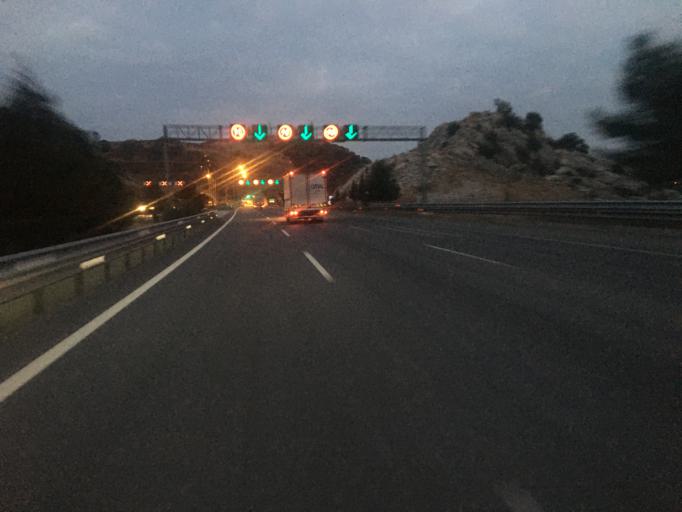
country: TR
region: Osmaniye
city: Haruniye
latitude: 37.1799
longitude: 36.4446
